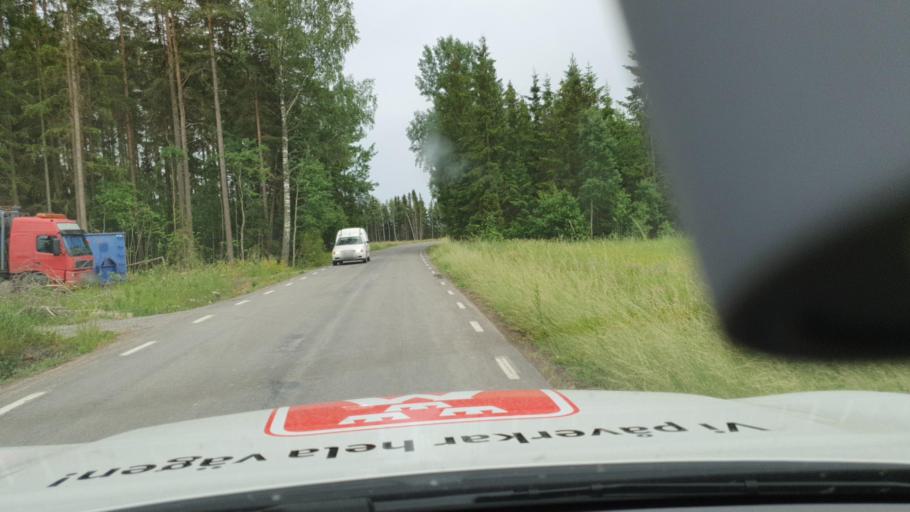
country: SE
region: Vaestra Goetaland
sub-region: Tidaholms Kommun
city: Olofstorp
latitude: 58.3124
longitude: 14.0636
